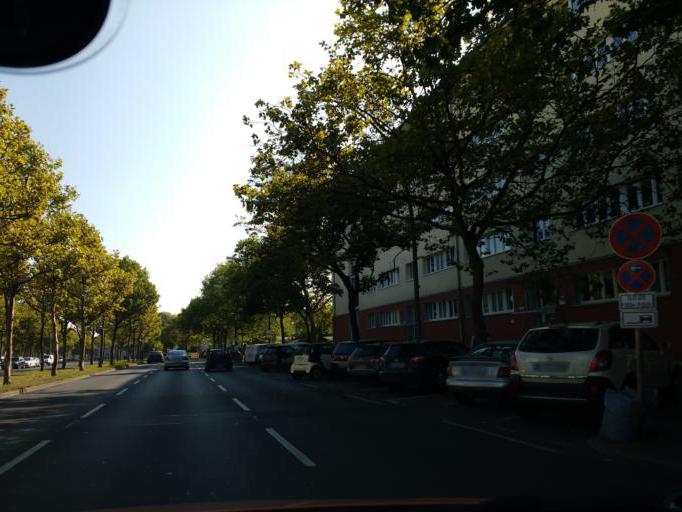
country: DE
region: Berlin
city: Halensee
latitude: 52.4882
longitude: 13.3044
